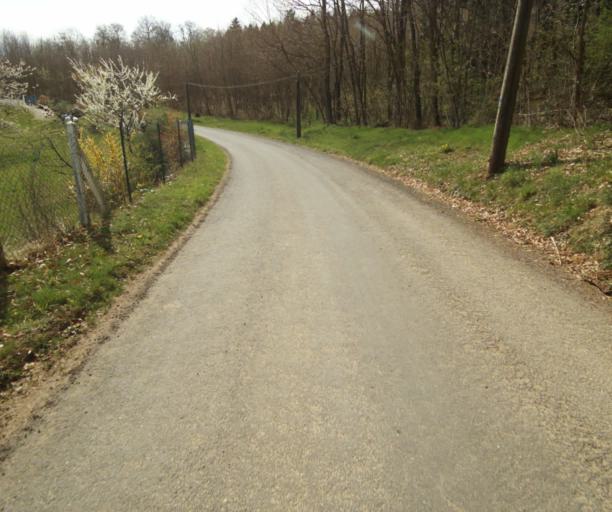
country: FR
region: Limousin
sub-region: Departement de la Correze
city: Naves
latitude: 45.3344
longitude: 1.7673
